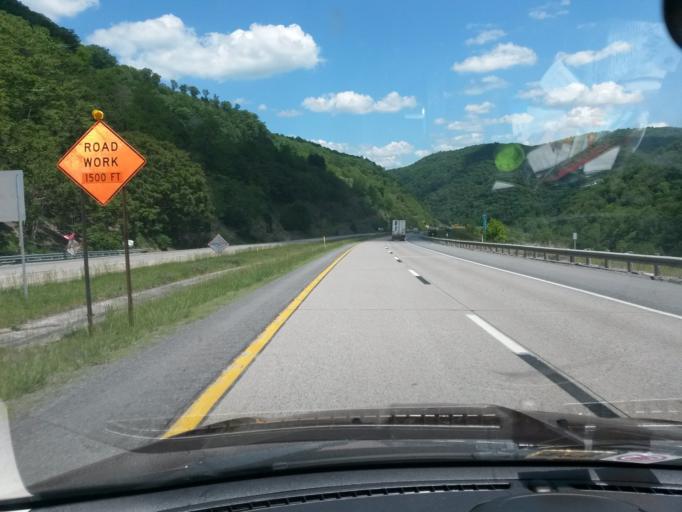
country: US
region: West Virginia
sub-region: Summers County
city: Hinton
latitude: 37.7819
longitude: -80.9437
